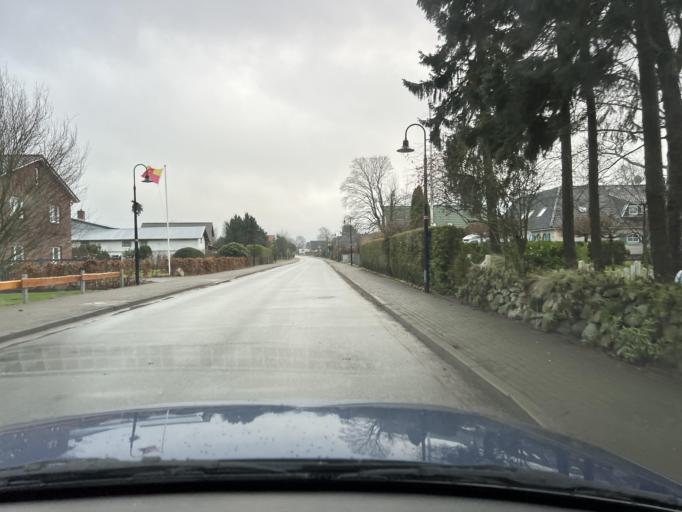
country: DE
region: Schleswig-Holstein
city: Lohe-Rickelshof
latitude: 54.2118
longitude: 9.0733
